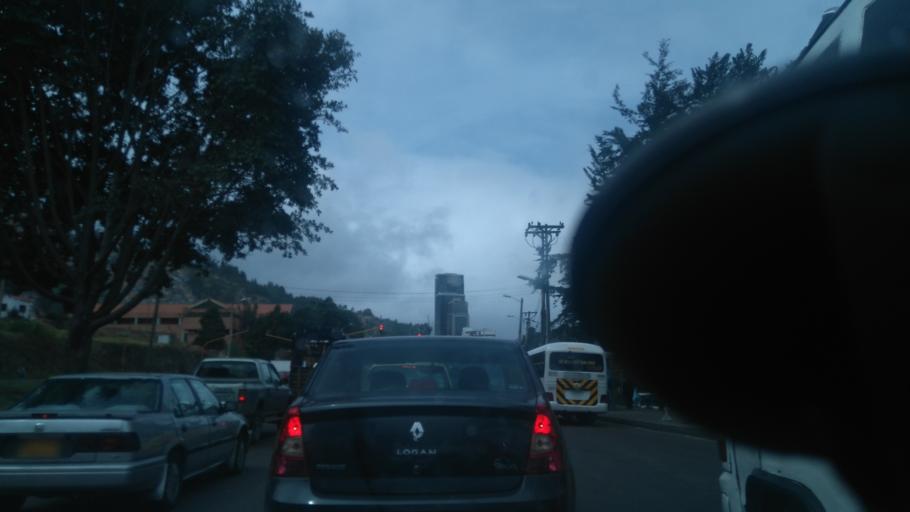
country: CO
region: Cundinamarca
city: La Calera
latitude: 4.7417
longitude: -74.0225
